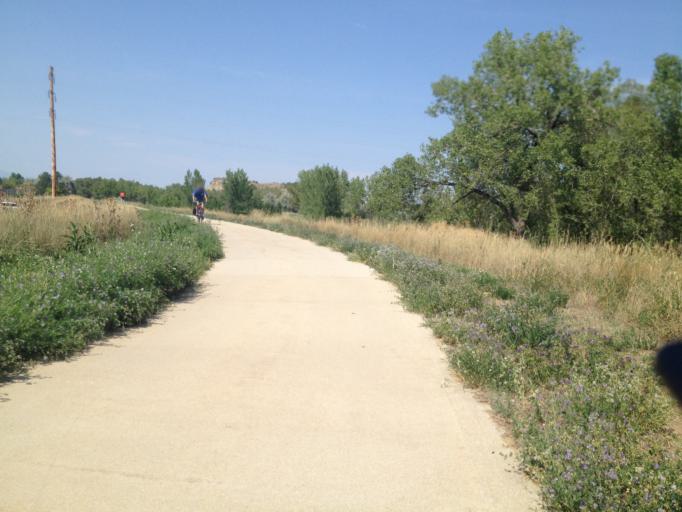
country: US
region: Colorado
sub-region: Boulder County
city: Boulder
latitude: 40.0191
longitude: -105.2161
